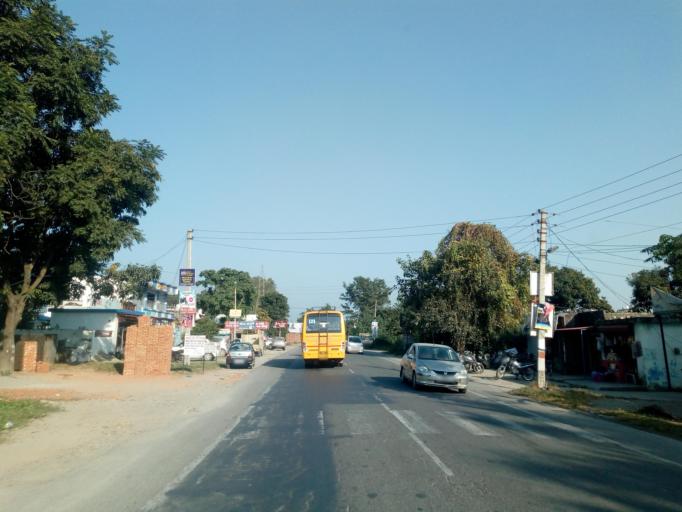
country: IN
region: Uttarakhand
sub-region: Dehradun
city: Dehradun
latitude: 30.3445
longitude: 77.9259
